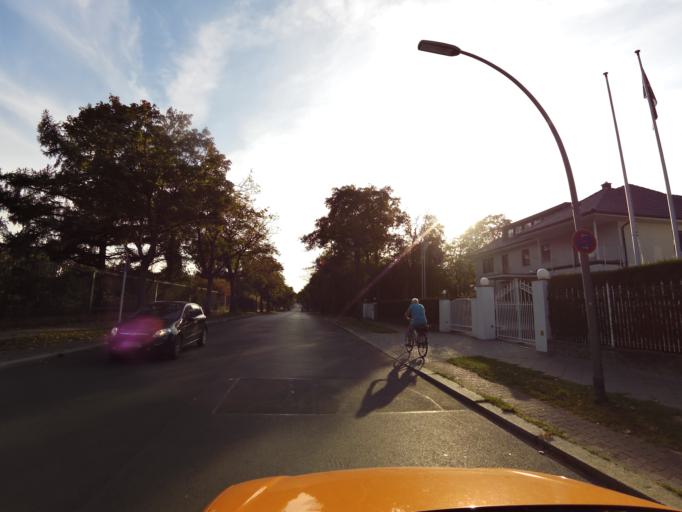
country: DE
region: Berlin
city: Dahlem
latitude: 52.4556
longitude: 13.3004
